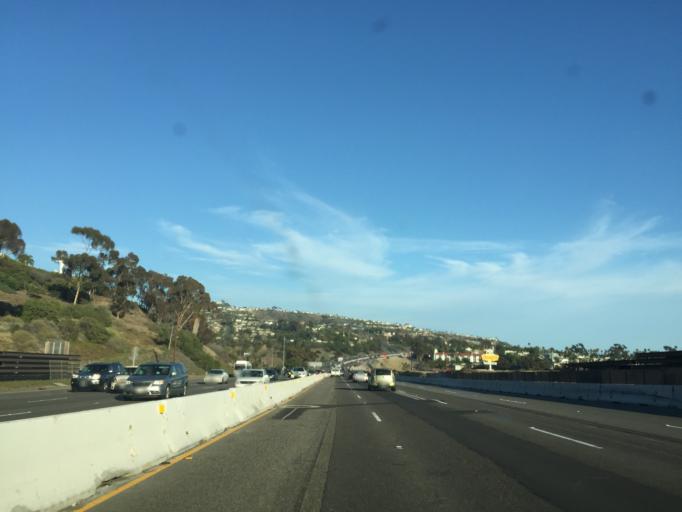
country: US
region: California
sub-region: Orange County
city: San Clemente
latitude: 33.4408
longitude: -117.6258
